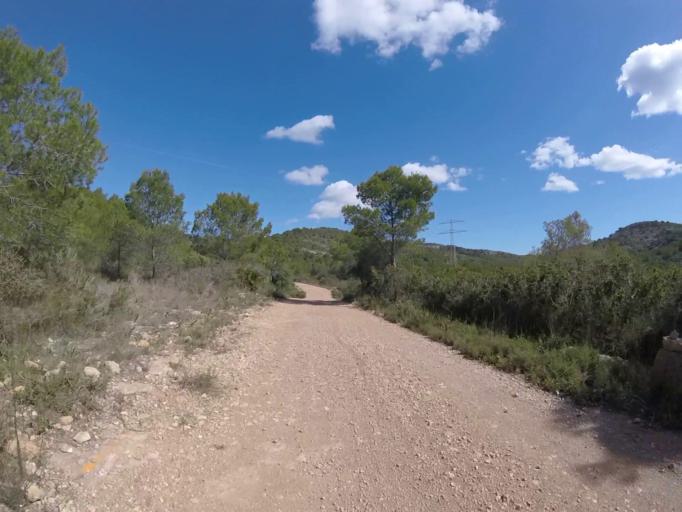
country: ES
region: Valencia
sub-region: Provincia de Castello
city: Alcoceber
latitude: 40.2886
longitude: 0.3182
